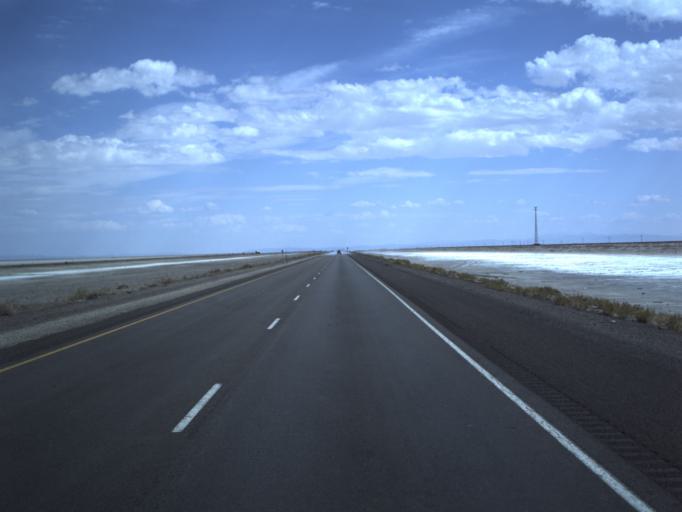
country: US
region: Utah
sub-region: Tooele County
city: Wendover
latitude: 40.7376
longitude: -113.8097
